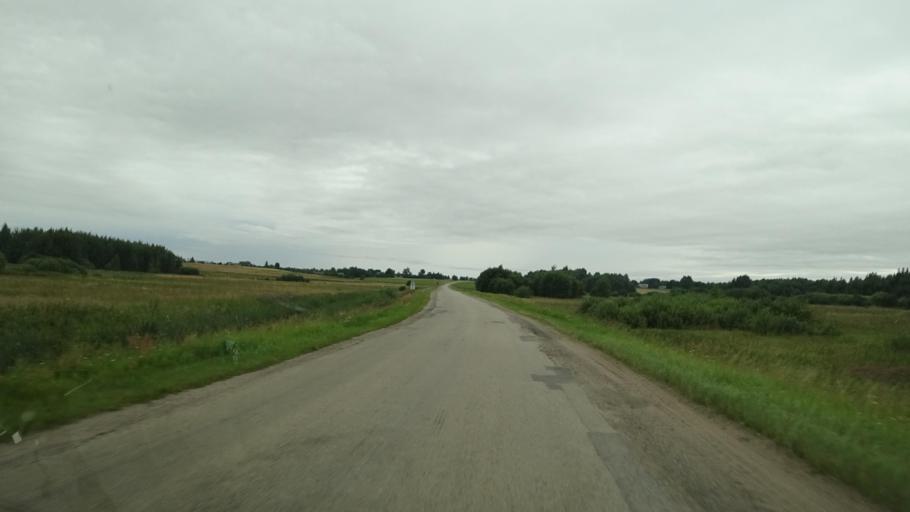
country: LT
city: Kelme
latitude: 55.4011
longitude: 22.8673
